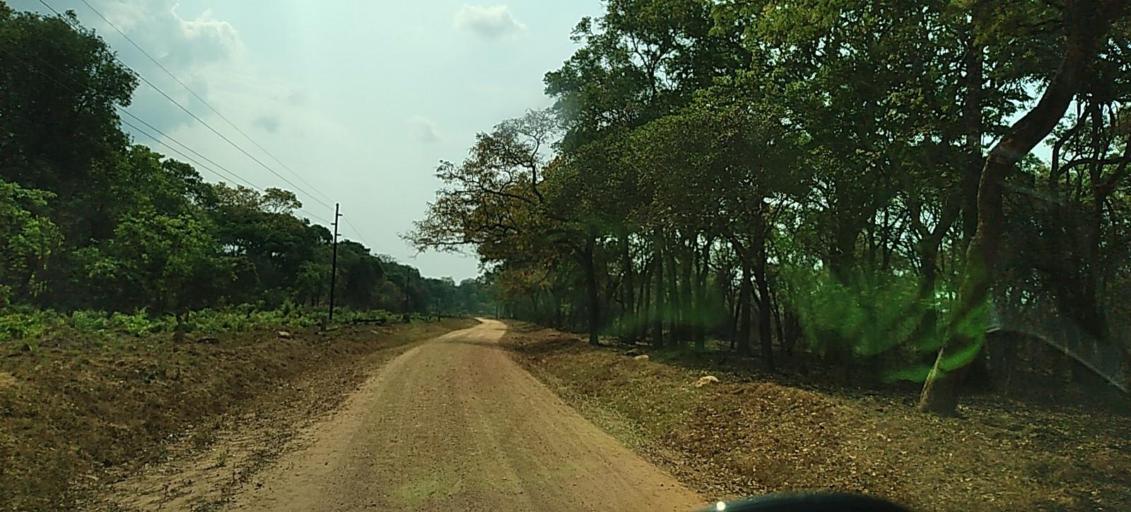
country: ZM
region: North-Western
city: Solwezi
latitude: -12.7109
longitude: 26.4245
